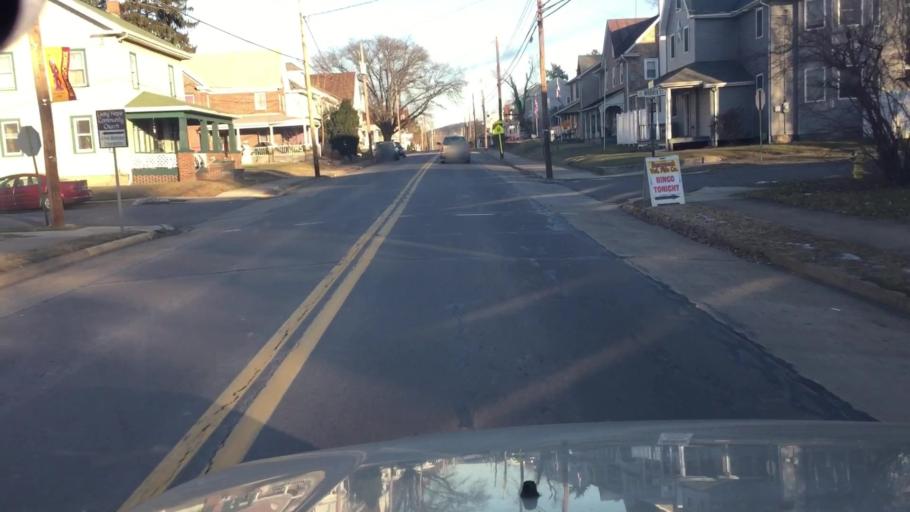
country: US
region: Pennsylvania
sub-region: Luzerne County
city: Nescopeck
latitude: 41.0523
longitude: -76.2188
